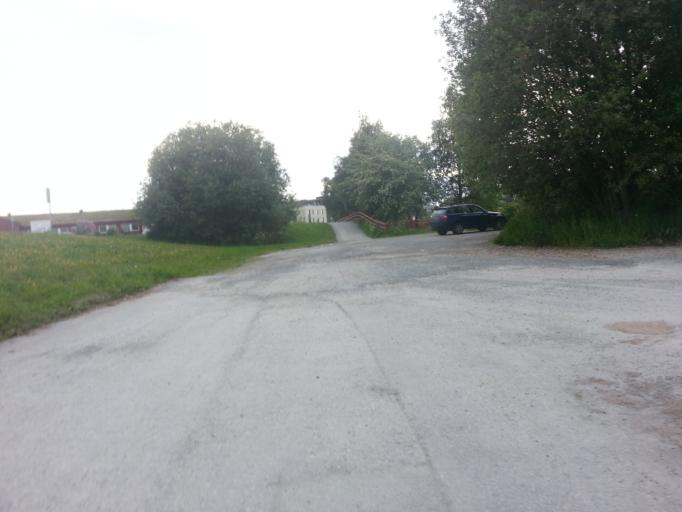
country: NO
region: Sor-Trondelag
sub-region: Trondheim
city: Trondheim
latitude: 63.4118
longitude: 10.4426
